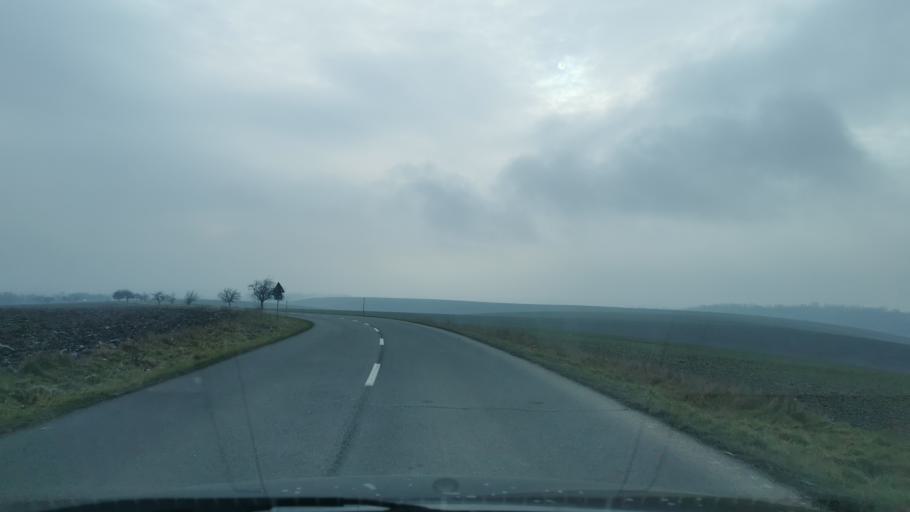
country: SK
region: Trnavsky
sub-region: Okres Senica
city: Senica
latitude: 48.7169
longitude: 17.3231
